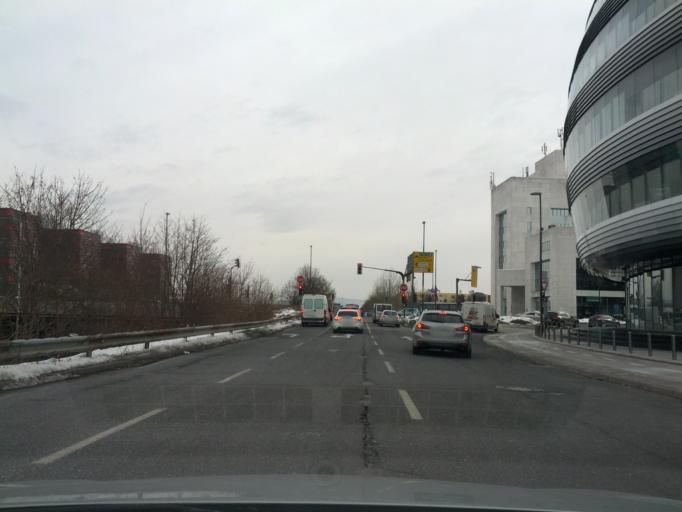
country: SI
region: Ljubljana
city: Ljubljana
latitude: 46.0834
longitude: 14.5123
